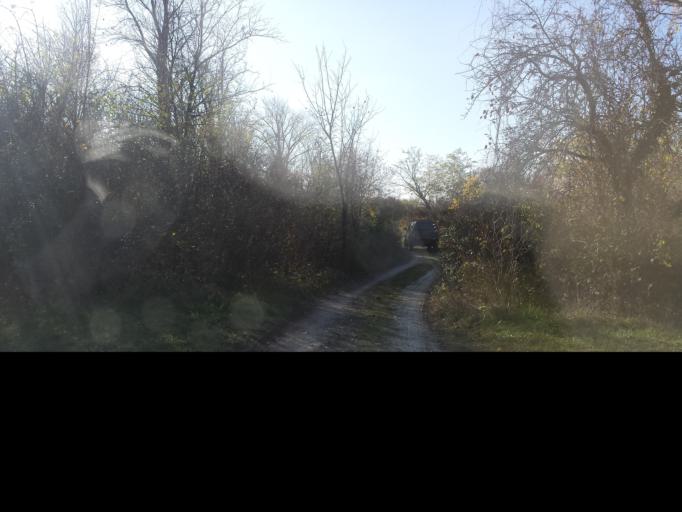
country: IT
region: Friuli Venezia Giulia
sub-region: Provincia di Udine
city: Percoto
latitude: 45.9826
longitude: 13.3319
